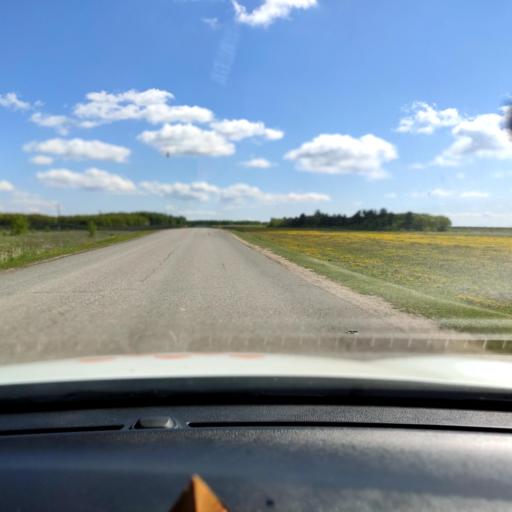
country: RU
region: Tatarstan
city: Kuybyshevskiy Zaton
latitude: 55.3423
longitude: 49.0717
